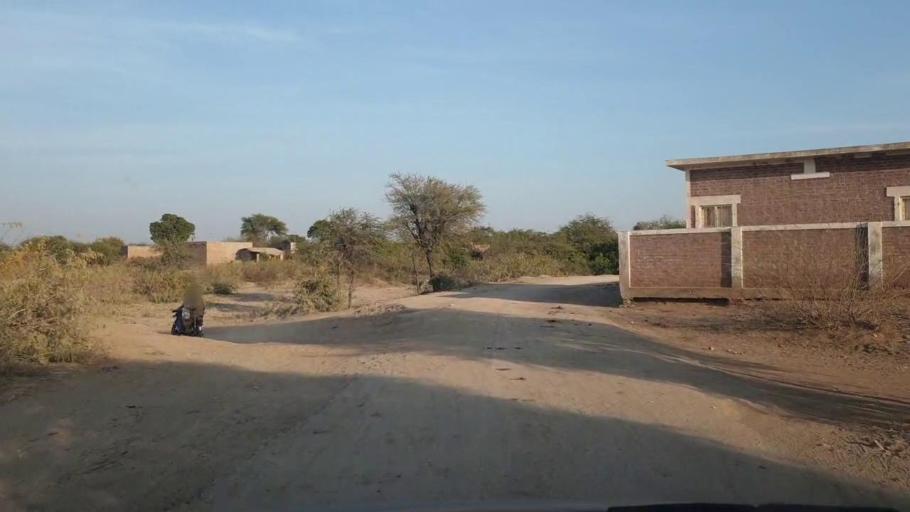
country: PK
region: Sindh
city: Chambar
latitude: 25.2574
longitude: 68.8061
